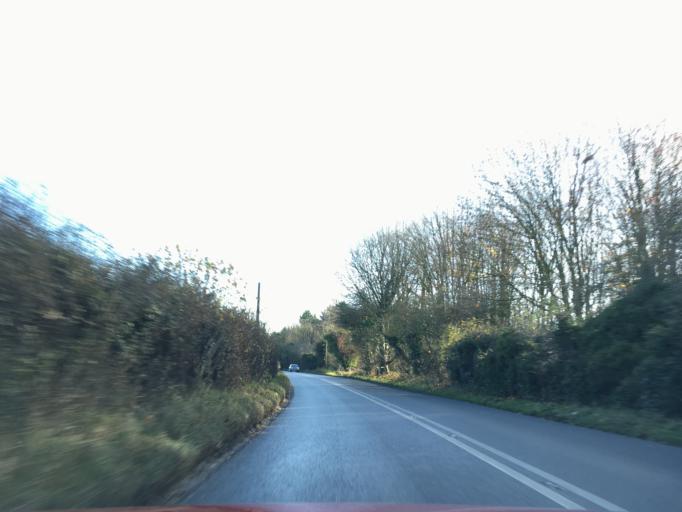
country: GB
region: England
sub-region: Wiltshire
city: Tidworth
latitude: 51.2587
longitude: -1.6342
